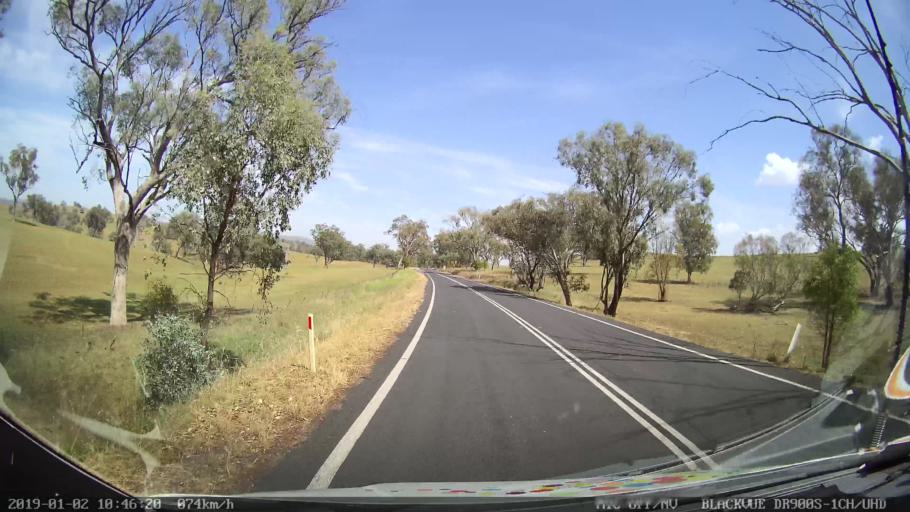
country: AU
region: New South Wales
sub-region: Cootamundra
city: Cootamundra
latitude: -34.7522
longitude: 148.2885
